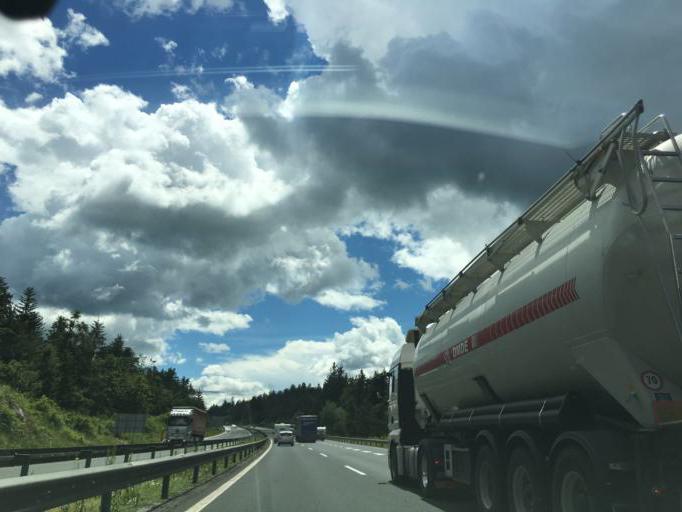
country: SI
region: Logatec
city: Logatec
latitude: 45.8958
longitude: 14.2560
